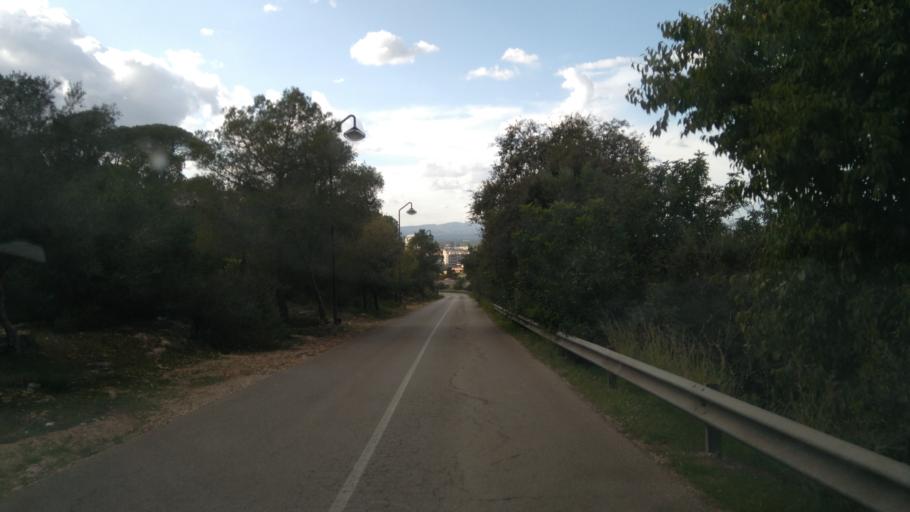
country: ES
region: Valencia
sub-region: Provincia de Valencia
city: Alzira
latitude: 39.1538
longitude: -0.4192
